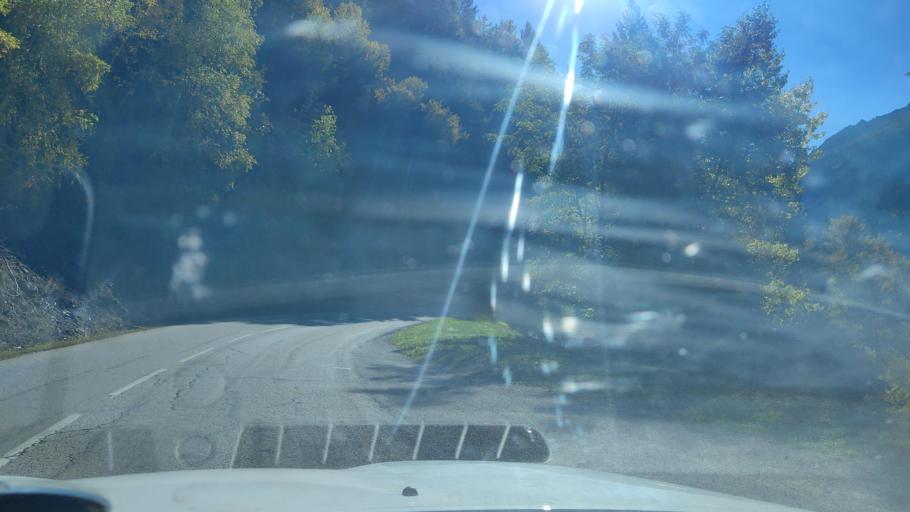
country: FR
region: Rhone-Alpes
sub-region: Departement de la Savoie
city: Seez
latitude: 45.6190
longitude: 6.8303
